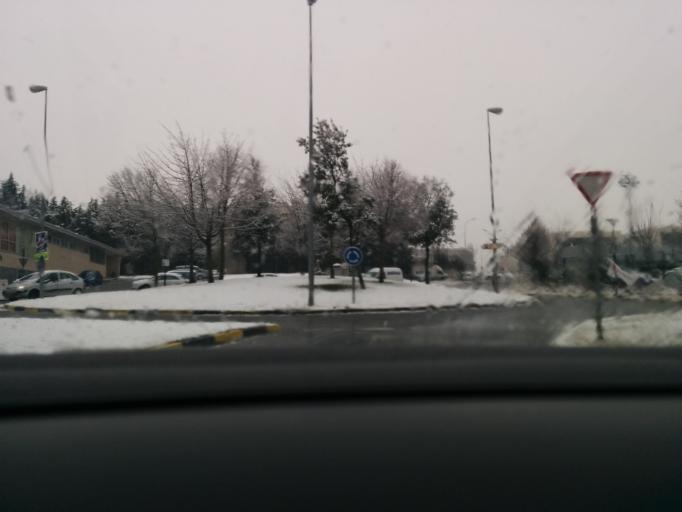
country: ES
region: Navarre
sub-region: Provincia de Navarra
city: Segundo Ensanche
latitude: 42.7890
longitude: -1.6210
